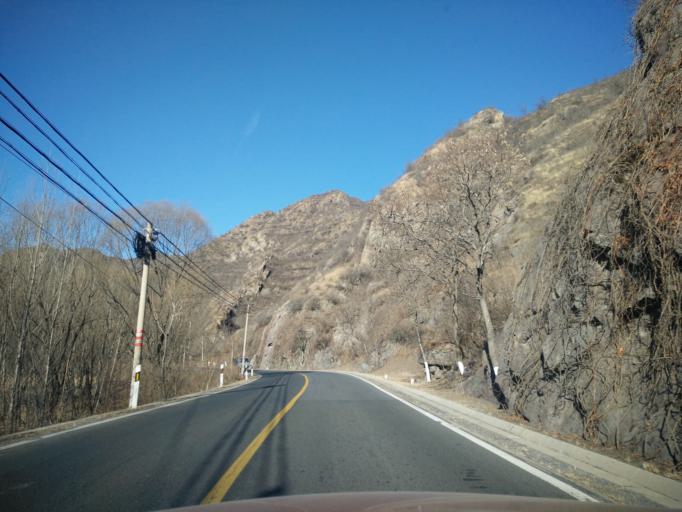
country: CN
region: Beijing
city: Yanchi
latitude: 40.0031
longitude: 115.7837
